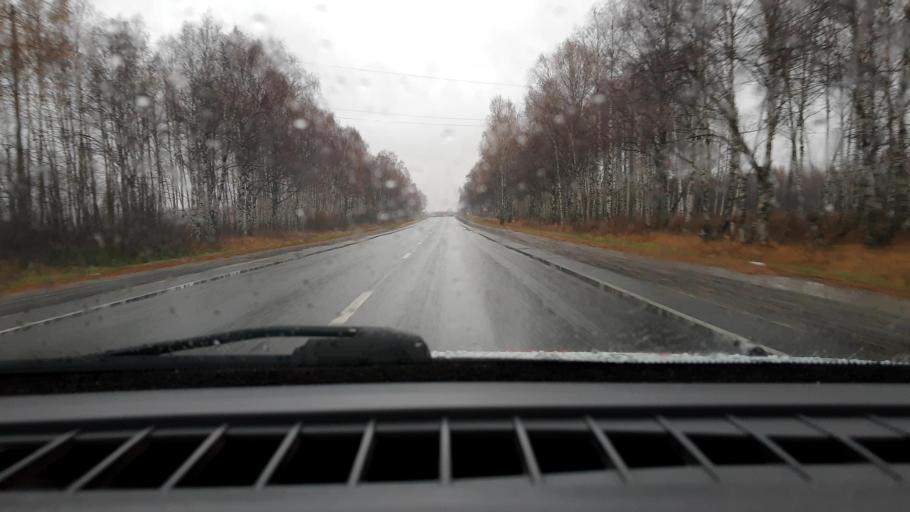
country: RU
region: Nizjnij Novgorod
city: Sitniki
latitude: 56.5193
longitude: 44.0254
